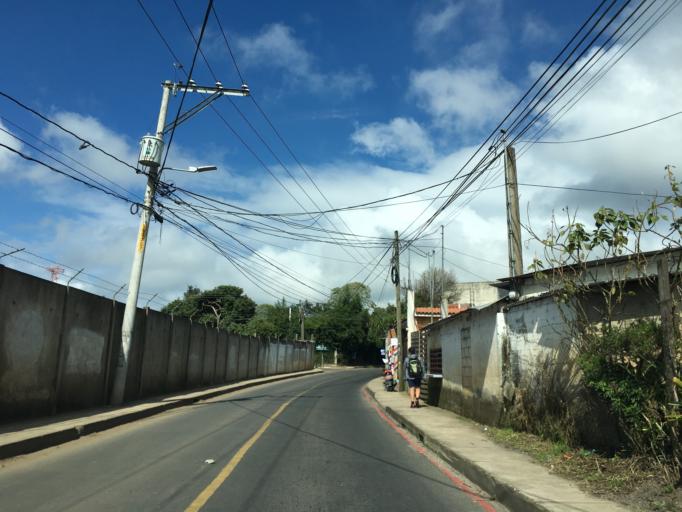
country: GT
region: Guatemala
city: San Jose Pinula
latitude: 14.5466
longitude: -90.4411
